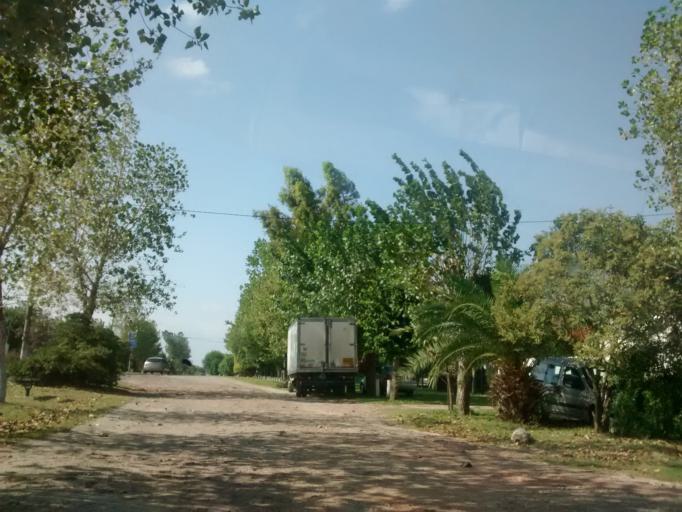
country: AR
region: Buenos Aires
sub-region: Partido de La Plata
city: La Plata
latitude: -35.0034
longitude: -57.8998
